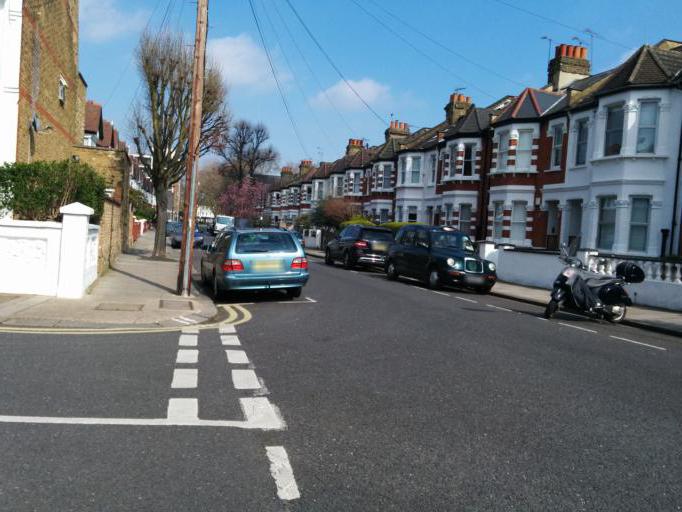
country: GB
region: England
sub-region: Greater London
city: Hammersmith
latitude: 51.4823
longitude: -0.2213
